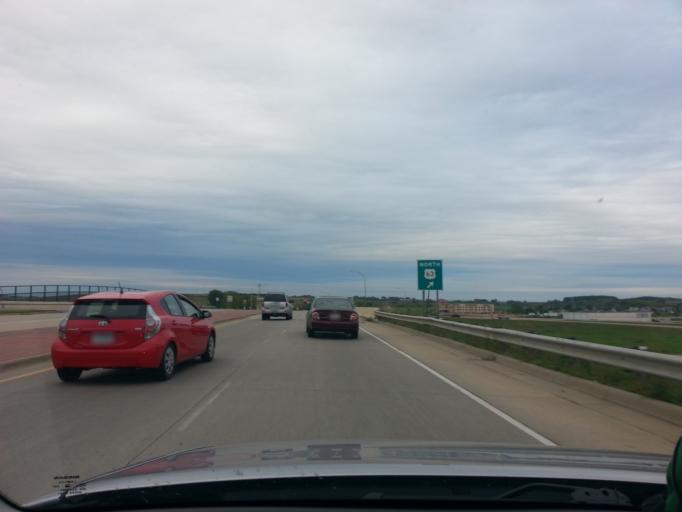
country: US
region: Minnesota
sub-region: Olmsted County
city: Rochester
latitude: 43.9637
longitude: -92.4646
